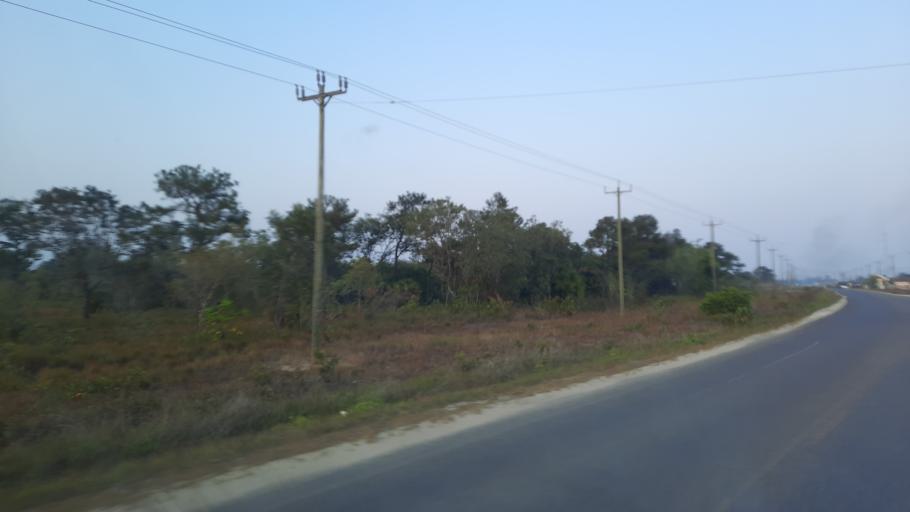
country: BZ
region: Stann Creek
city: Placencia
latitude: 16.5351
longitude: -88.4338
